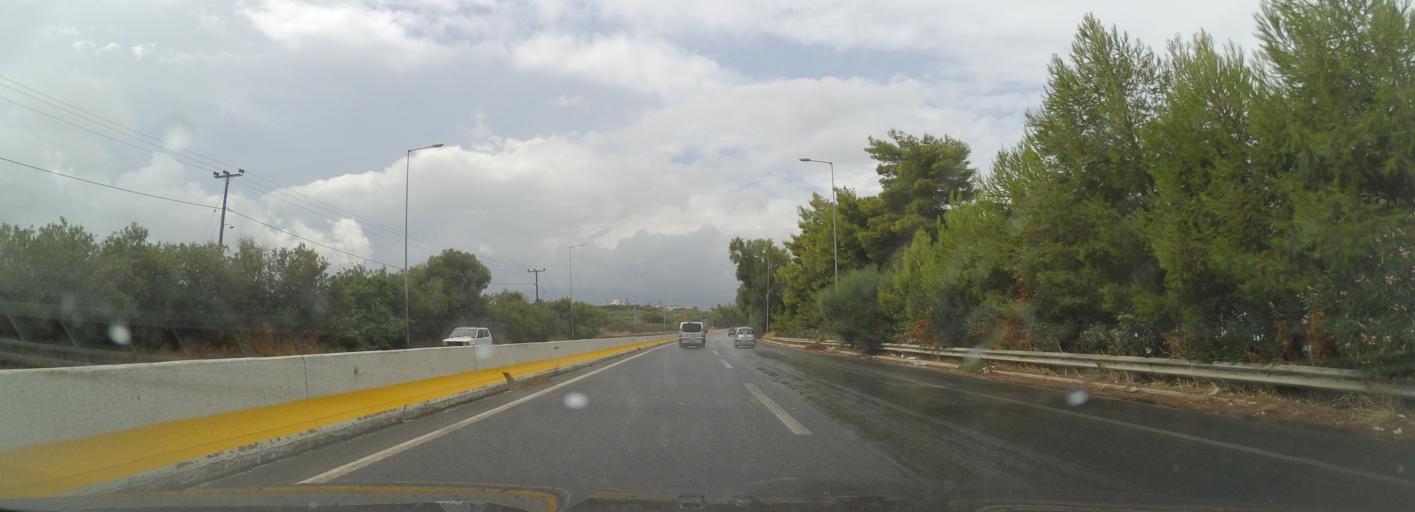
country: GR
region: Crete
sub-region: Nomos Irakleiou
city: Gazi
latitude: 35.3179
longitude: 25.0824
